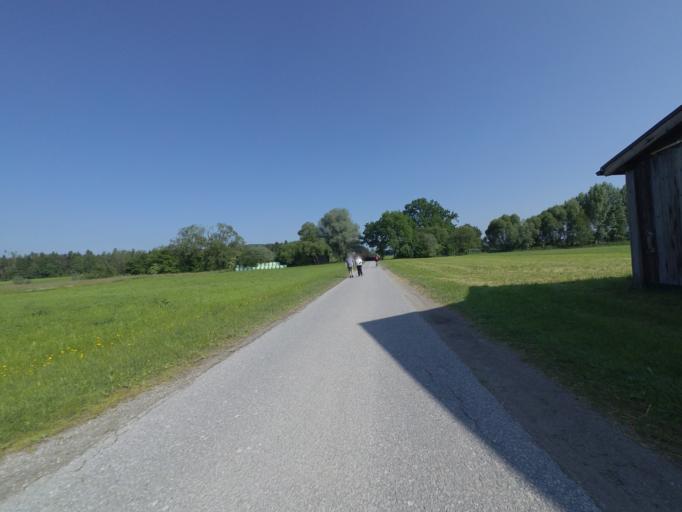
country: DE
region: Bavaria
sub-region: Upper Bavaria
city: Piding
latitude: 47.7655
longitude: 12.9671
